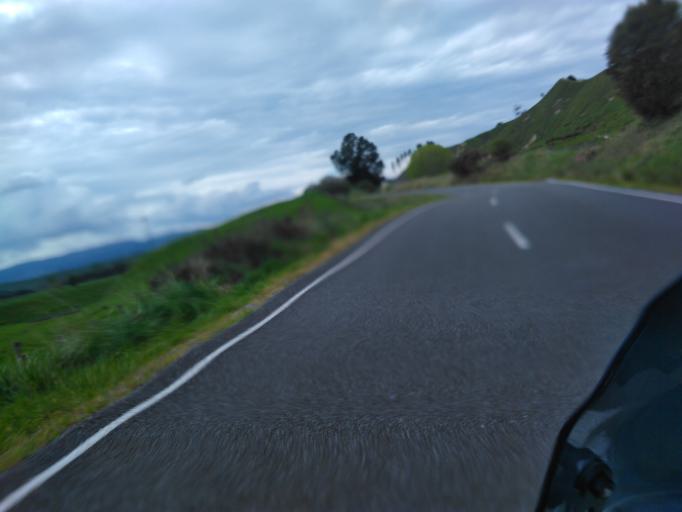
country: NZ
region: Hawke's Bay
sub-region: Wairoa District
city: Wairoa
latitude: -38.9236
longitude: 177.4273
